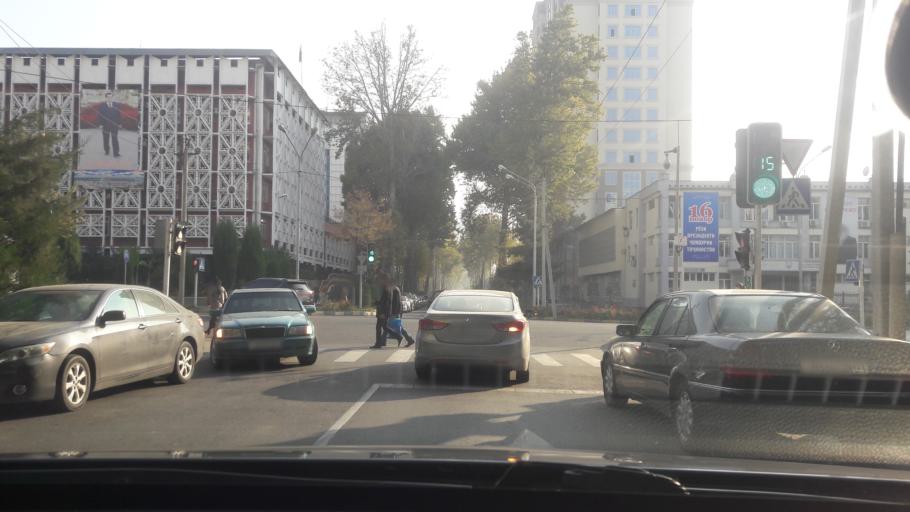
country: TJ
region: Dushanbe
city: Dushanbe
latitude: 38.5791
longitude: 68.7894
